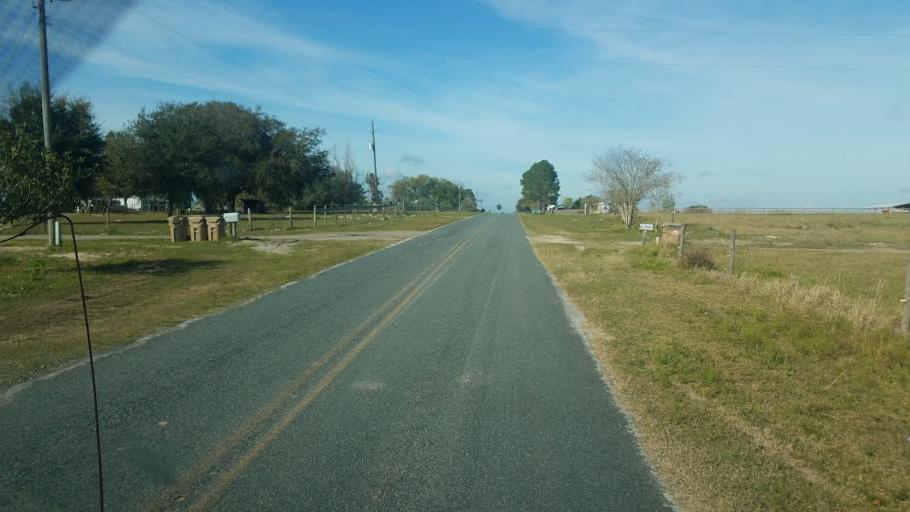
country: US
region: Florida
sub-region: Lake County
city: Clermont
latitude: 28.4452
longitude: -81.7943
